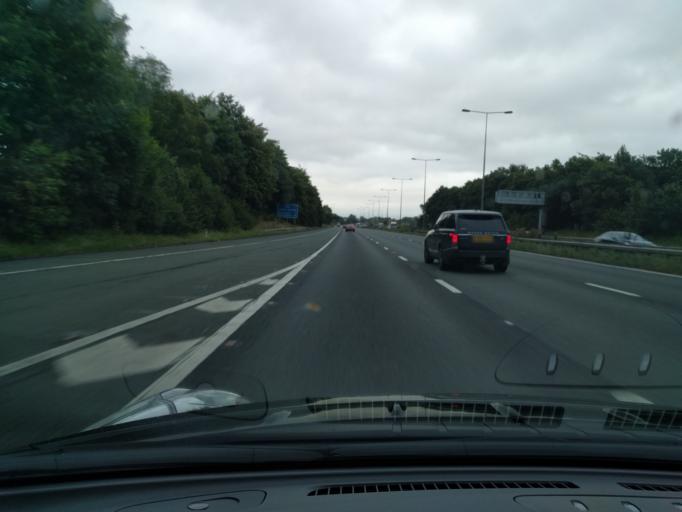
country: GB
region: England
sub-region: St. Helens
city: Newton-le-Willows
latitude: 53.4632
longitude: -2.6192
